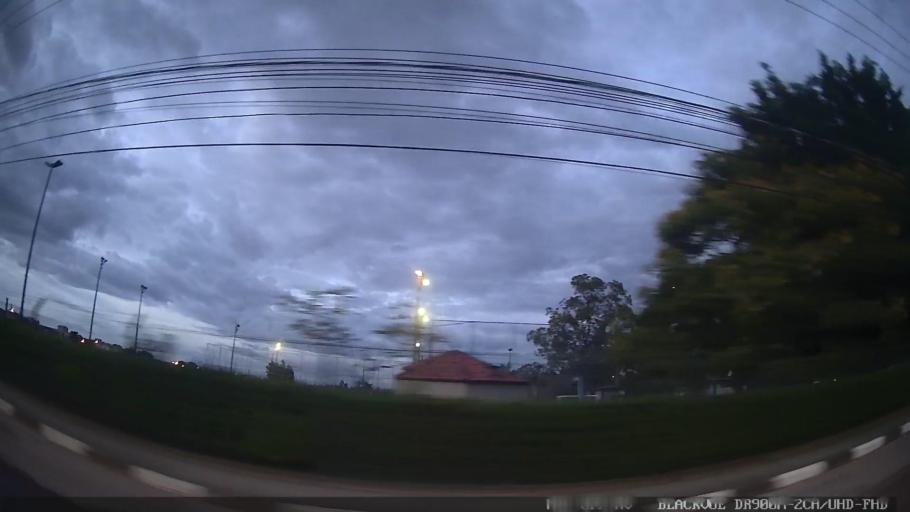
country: BR
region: Sao Paulo
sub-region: Suzano
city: Suzano
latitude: -23.5411
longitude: -46.2745
